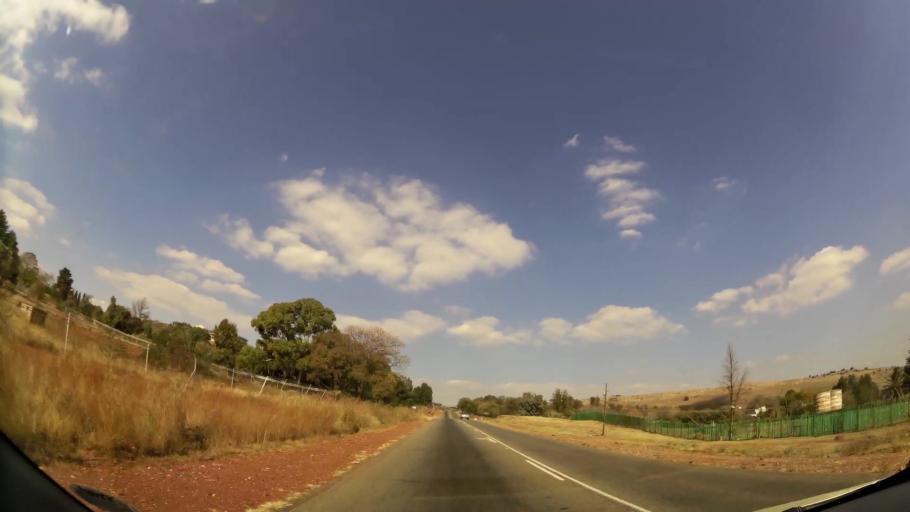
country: ZA
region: Gauteng
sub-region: West Rand District Municipality
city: Krugersdorp
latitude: -26.0406
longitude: 27.7429
